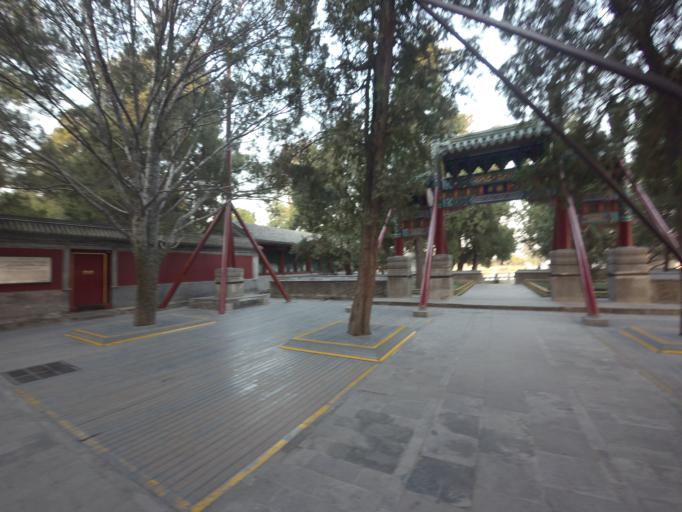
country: CN
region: Beijing
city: Haidian
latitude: 39.9898
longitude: 116.2702
